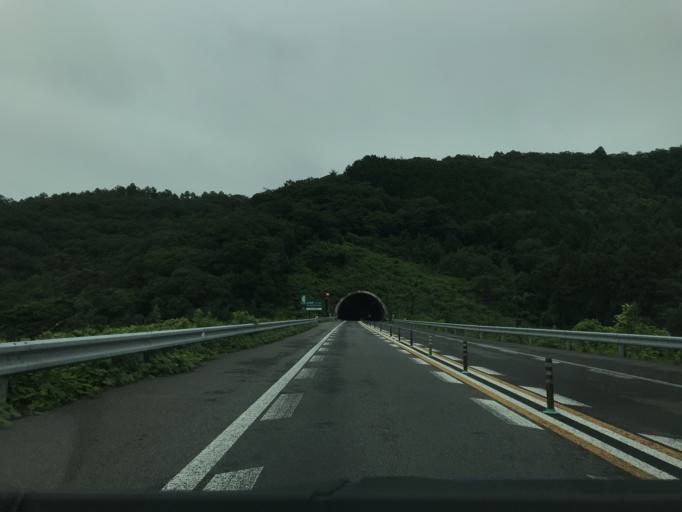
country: JP
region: Fukuoka
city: Nakatsu
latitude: 33.5176
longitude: 131.2692
